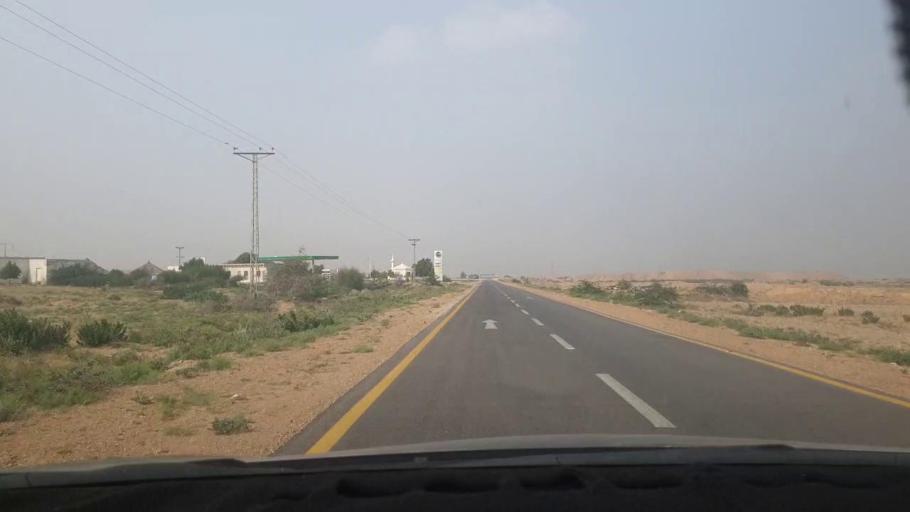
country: PK
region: Sindh
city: Jamshoro
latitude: 25.5698
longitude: 68.3158
